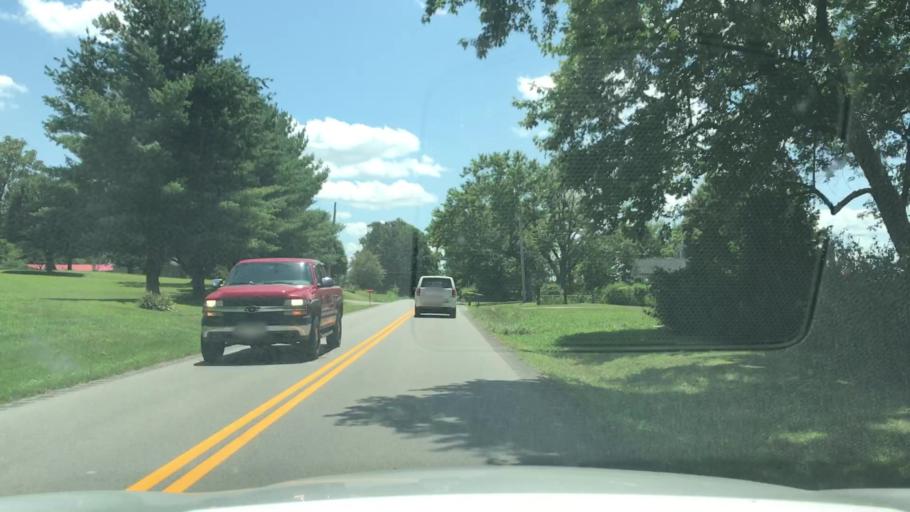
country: US
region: Kentucky
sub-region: Christian County
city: Hopkinsville
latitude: 36.9019
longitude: -87.4482
